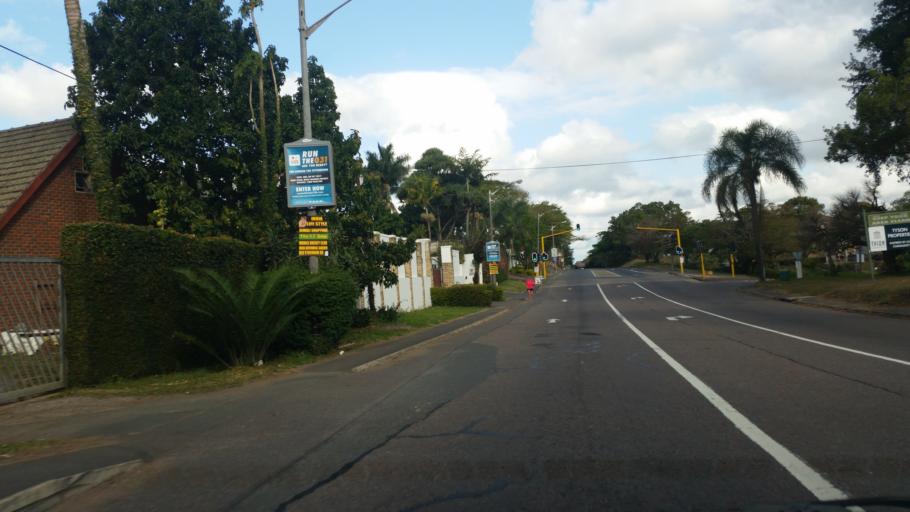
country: ZA
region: KwaZulu-Natal
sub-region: eThekwini Metropolitan Municipality
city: Berea
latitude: -29.8369
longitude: 30.9246
